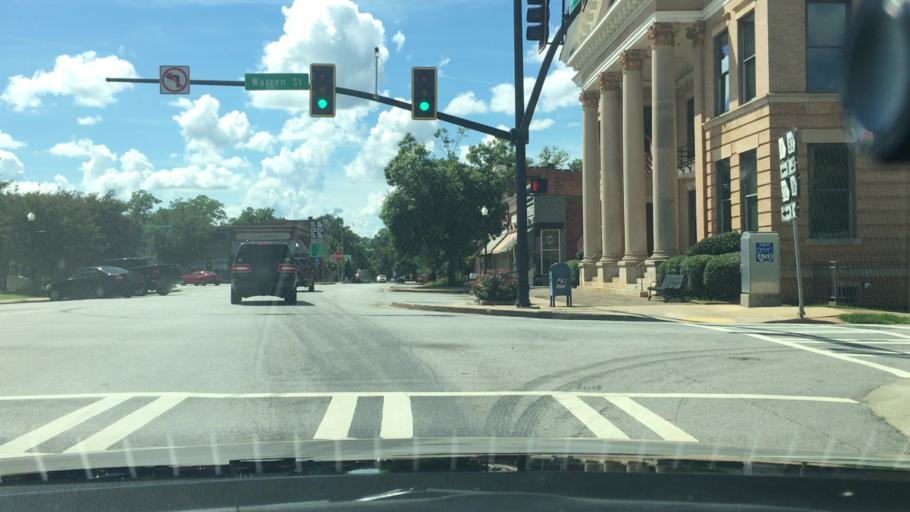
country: US
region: Georgia
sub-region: Jasper County
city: Monticello
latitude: 33.3046
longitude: -83.6834
